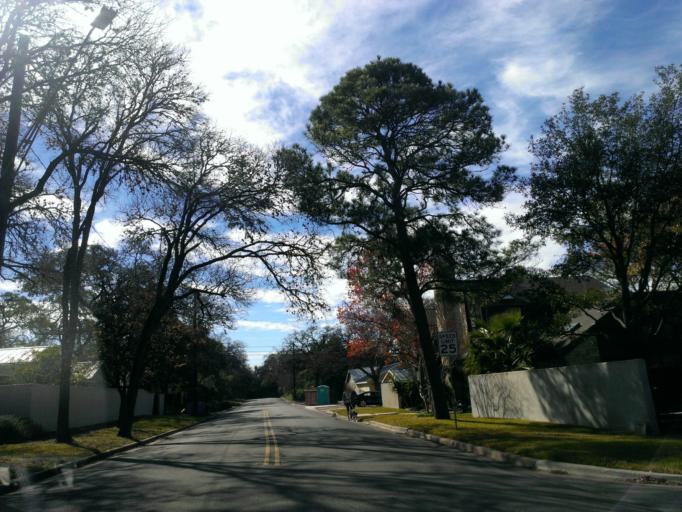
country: US
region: Texas
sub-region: Travis County
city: Rollingwood
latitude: 30.2948
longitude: -97.7763
